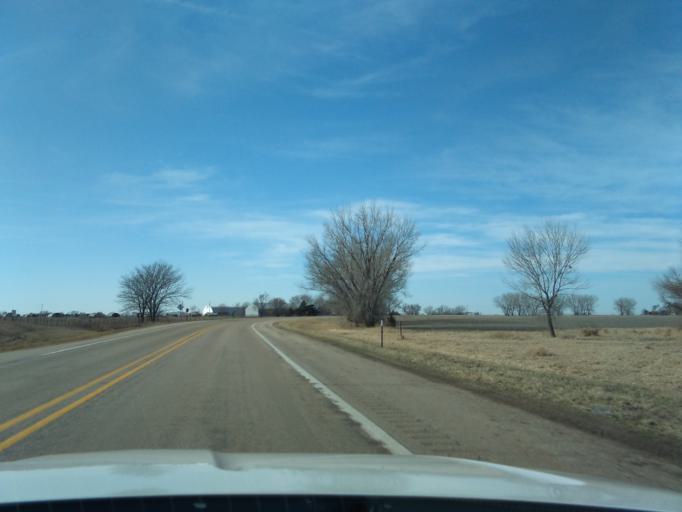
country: US
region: Nebraska
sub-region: Saline County
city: Friend
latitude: 40.6437
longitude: -97.4256
